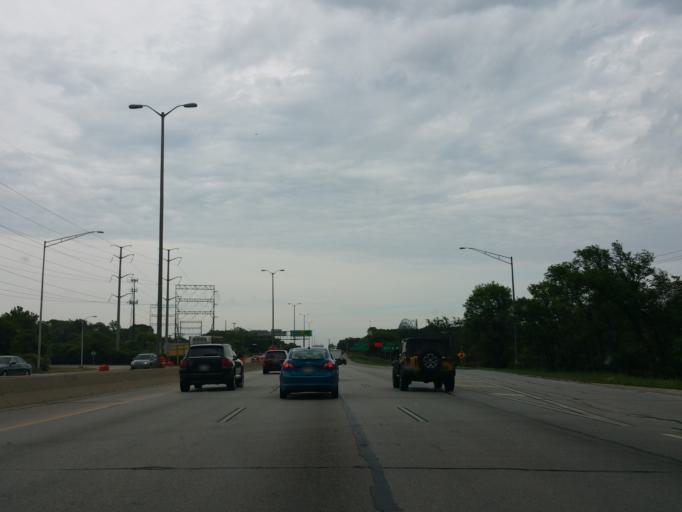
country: US
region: Wisconsin
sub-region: Milwaukee County
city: West Allis
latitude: 43.0303
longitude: -87.9903
